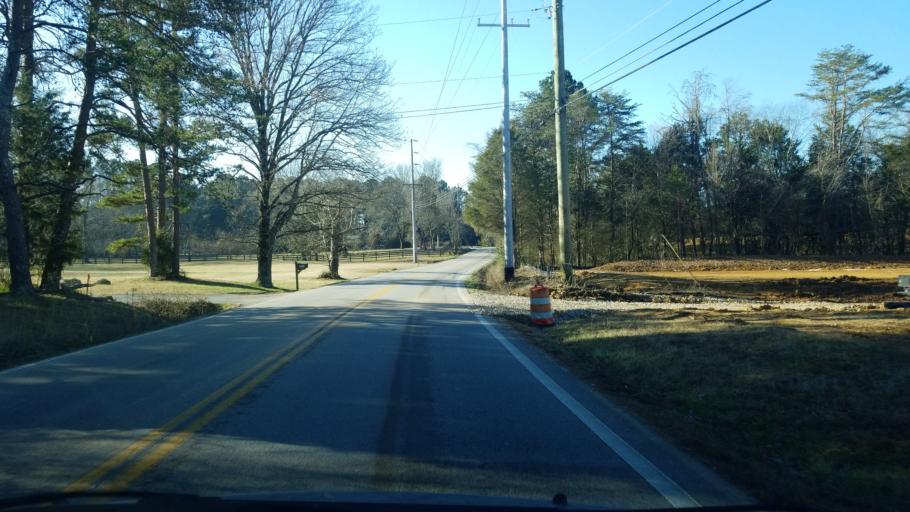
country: US
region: Tennessee
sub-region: Hamilton County
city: Collegedale
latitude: 35.0380
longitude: -85.0768
